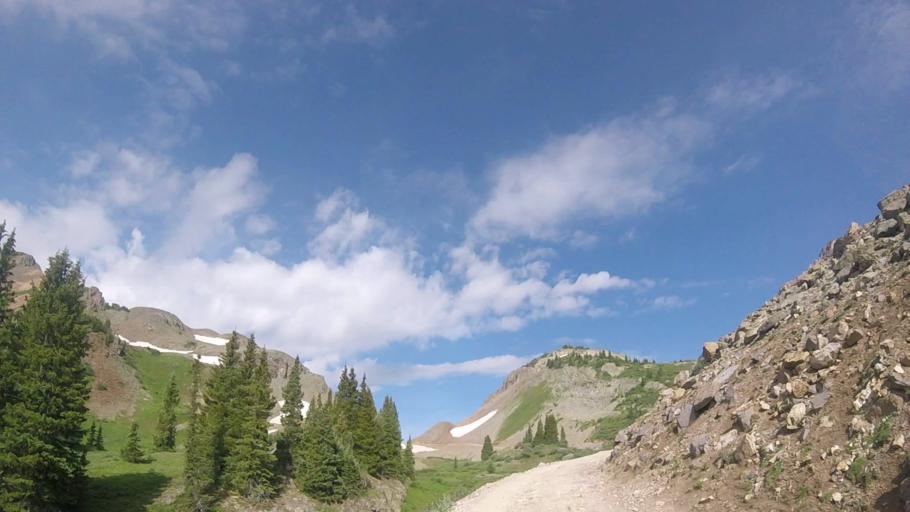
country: US
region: Colorado
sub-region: San Miguel County
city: Telluride
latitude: 37.8507
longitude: -107.7742
